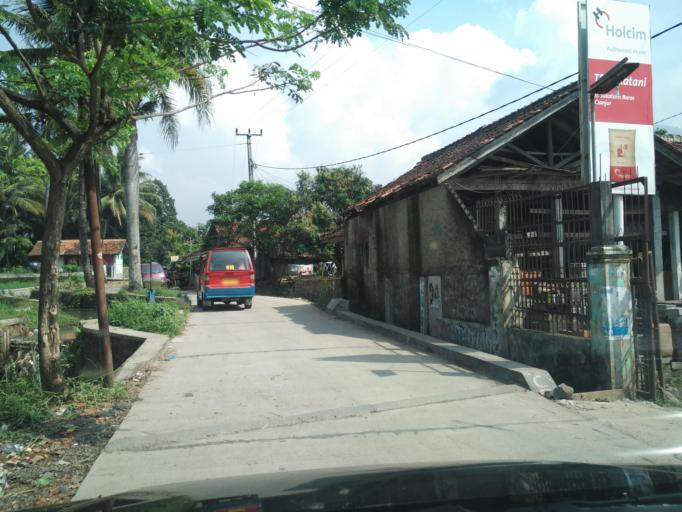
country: ID
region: West Java
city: Ciranjang-hilir
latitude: -6.7958
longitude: 107.1565
